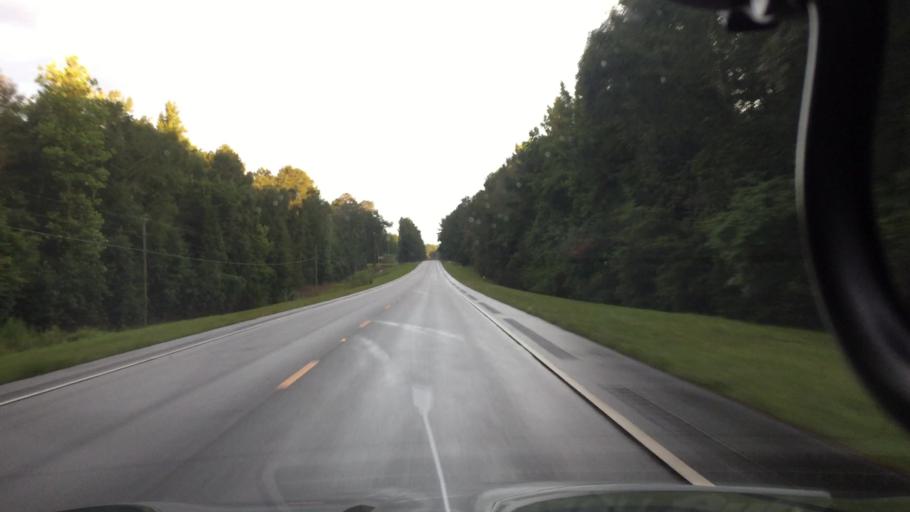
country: US
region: Alabama
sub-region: Coffee County
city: New Brockton
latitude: 31.5646
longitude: -85.9254
